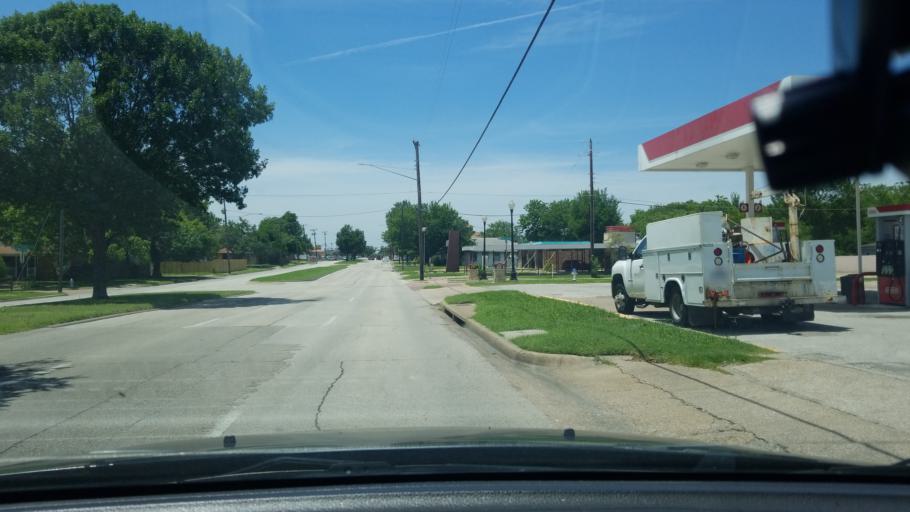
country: US
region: Texas
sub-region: Dallas County
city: Mesquite
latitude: 32.7887
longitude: -96.6081
